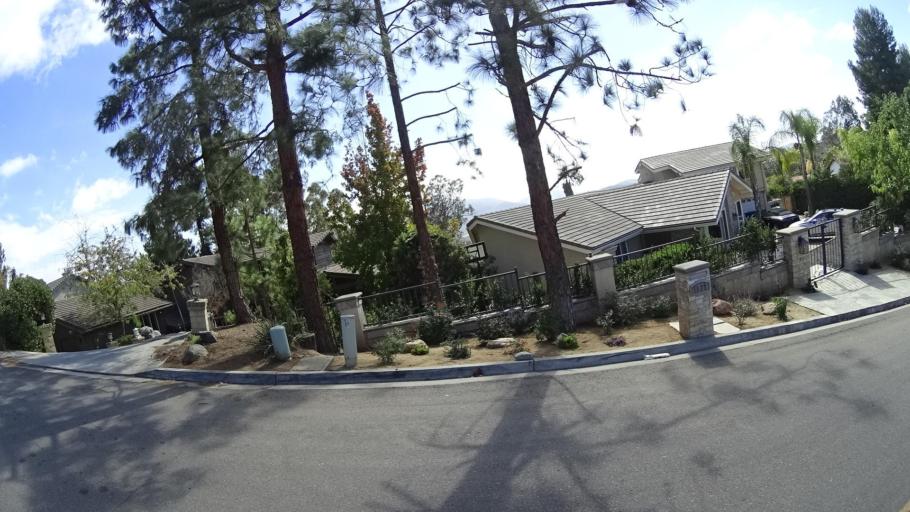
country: US
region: California
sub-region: San Diego County
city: Rancho San Diego
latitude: 32.7665
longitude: -116.9340
